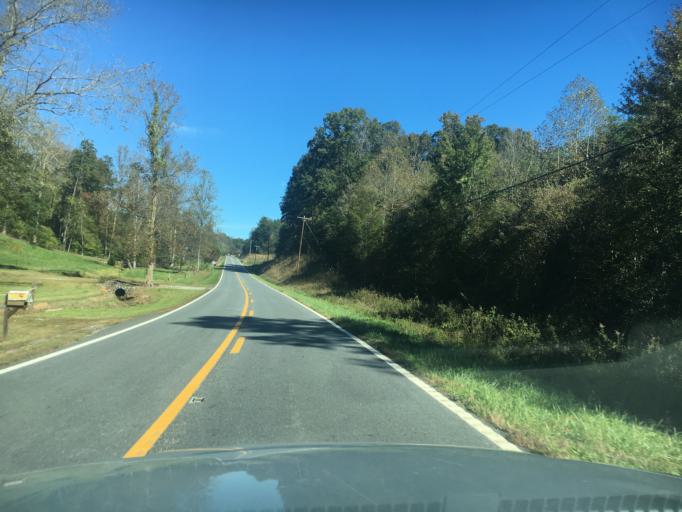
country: US
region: North Carolina
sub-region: Rutherford County
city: Spindale
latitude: 35.4912
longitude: -81.8667
